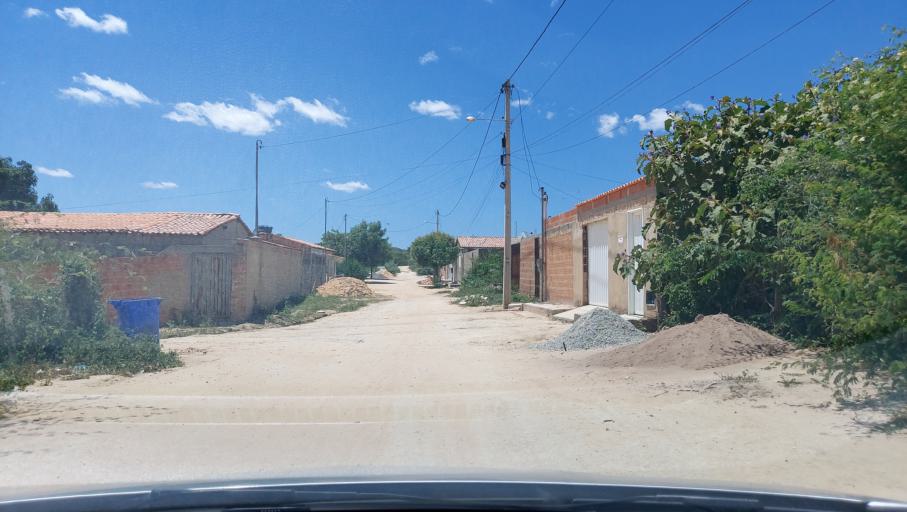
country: BR
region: Bahia
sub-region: Oliveira Dos Brejinhos
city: Beira Rio
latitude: -12.0070
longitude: -42.6302
